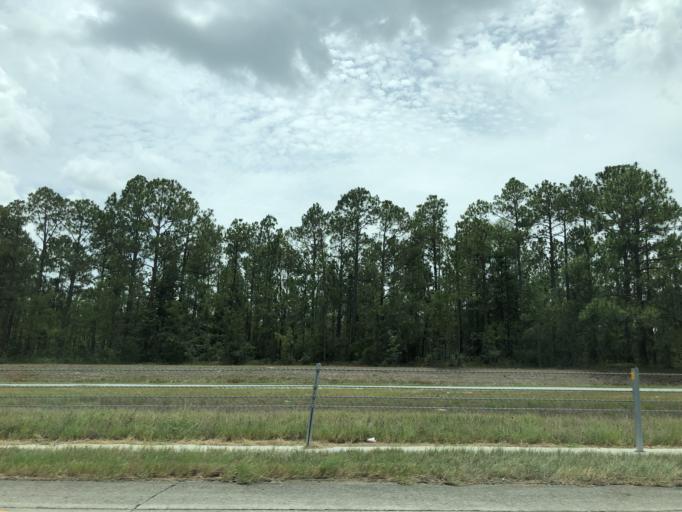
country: US
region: Georgia
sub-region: Toombs County
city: Lyons
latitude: 32.3883
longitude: -82.2703
